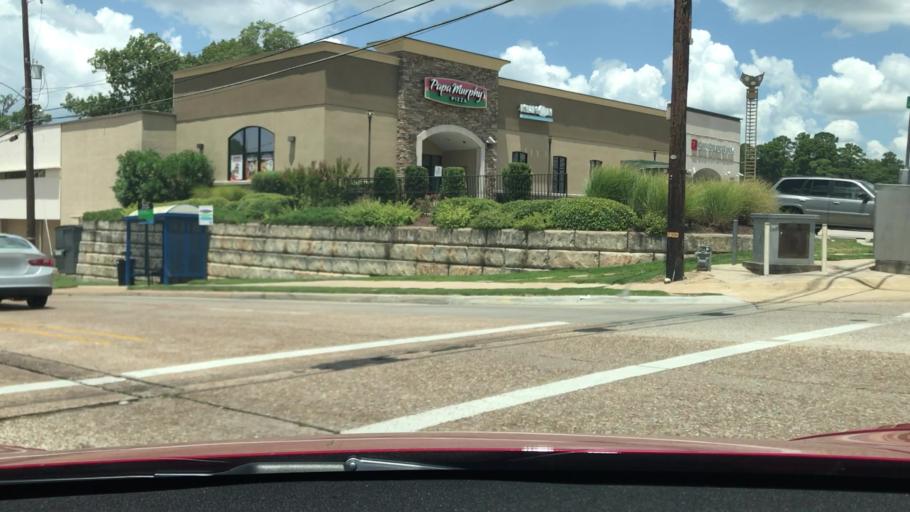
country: US
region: Louisiana
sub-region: Bossier Parish
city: Bossier City
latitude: 32.4547
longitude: -93.7461
